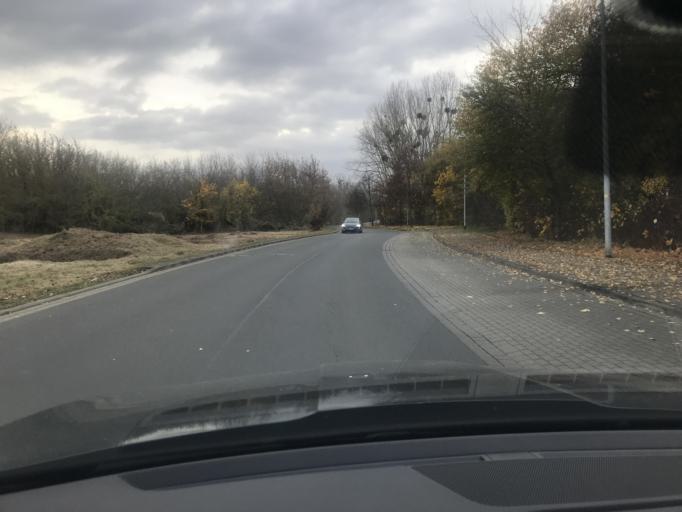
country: DE
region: Saxony-Anhalt
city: Quedlinburg
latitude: 51.7871
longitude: 11.1702
